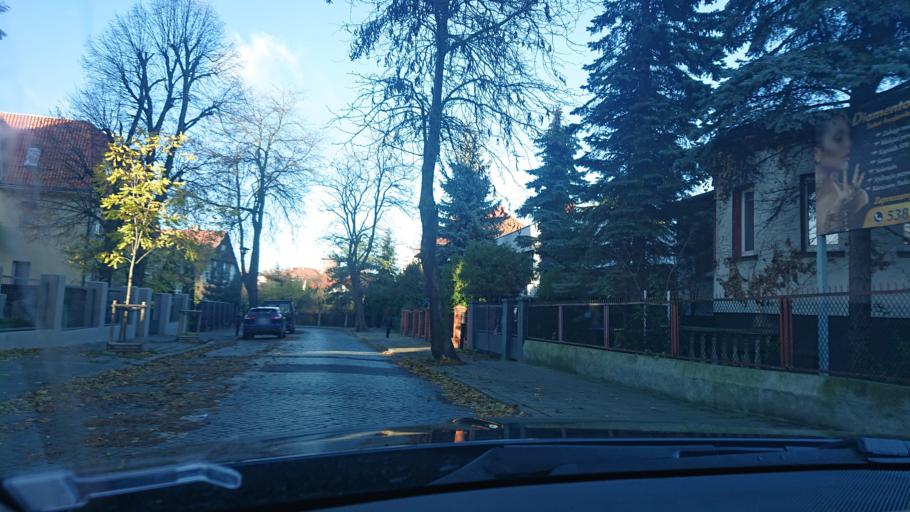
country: PL
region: Greater Poland Voivodeship
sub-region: Powiat gnieznienski
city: Gniezno
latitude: 52.5380
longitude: 17.6065
